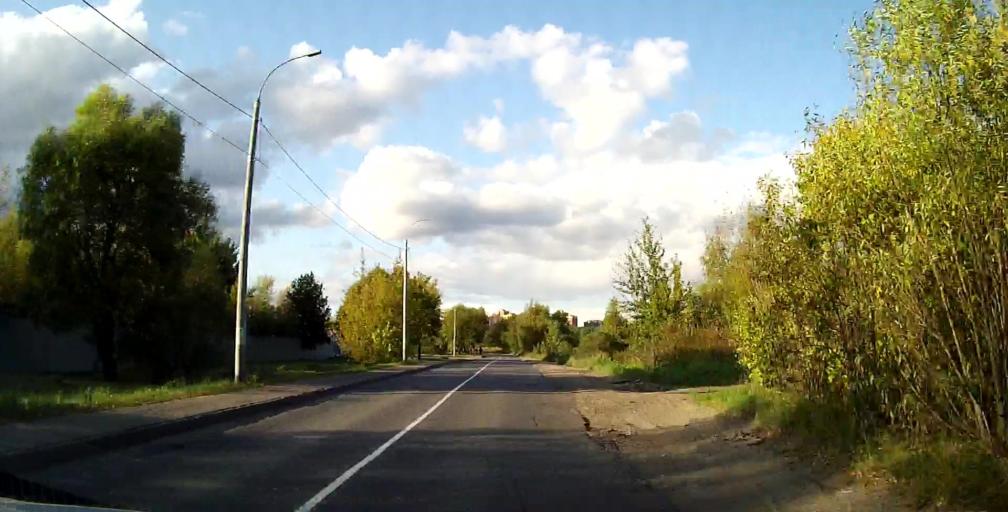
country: RU
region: Moskovskaya
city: Klimovsk
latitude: 55.3784
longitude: 37.5625
